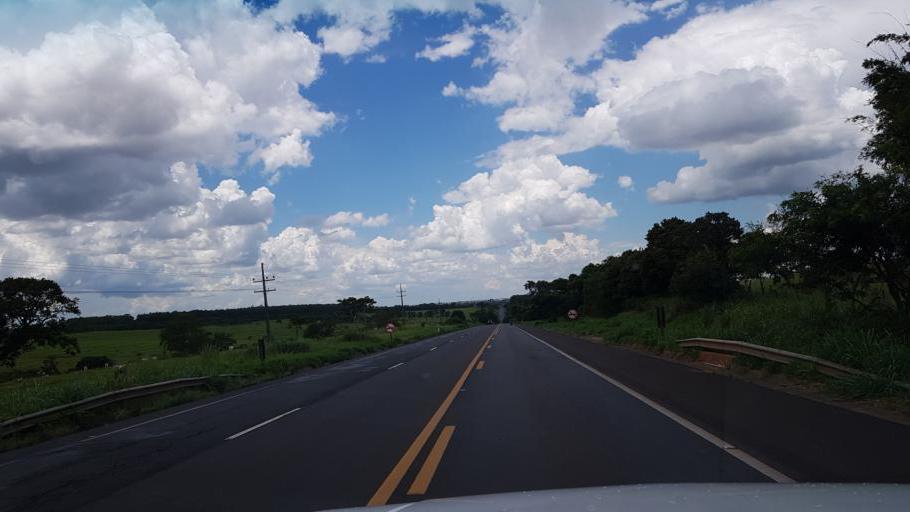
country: BR
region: Sao Paulo
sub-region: Paraguacu Paulista
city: Paraguacu Paulista
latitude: -22.3866
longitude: -50.6143
